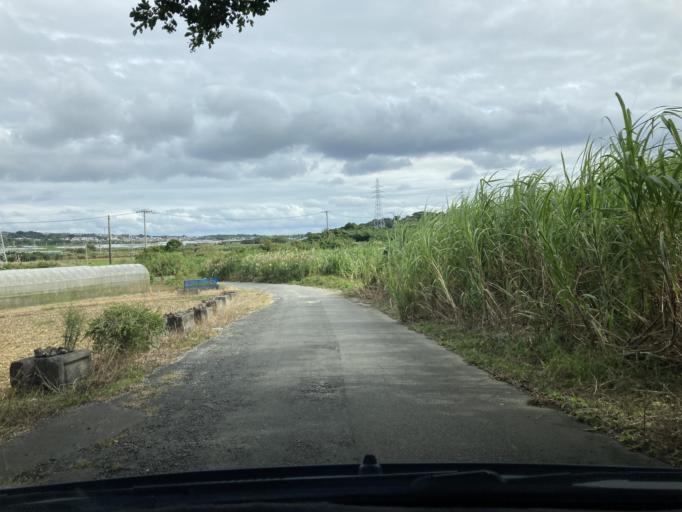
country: JP
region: Okinawa
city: Itoman
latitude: 26.1160
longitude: 127.6869
